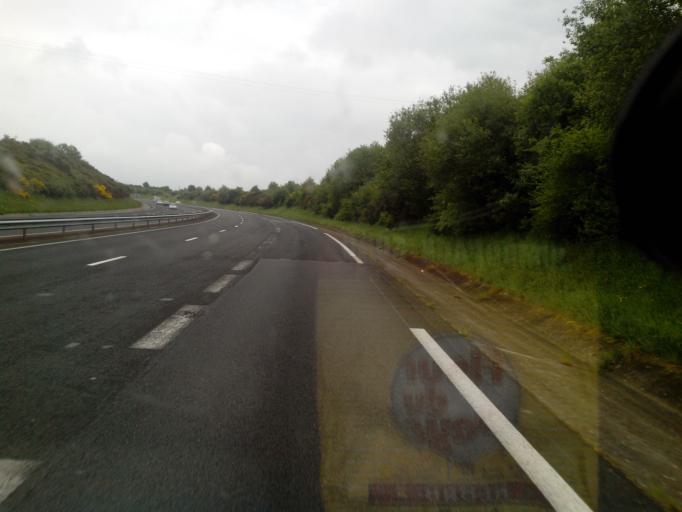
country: FR
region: Lower Normandy
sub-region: Departement de la Manche
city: Tessy-sur-Vire
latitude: 48.9476
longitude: -1.0181
